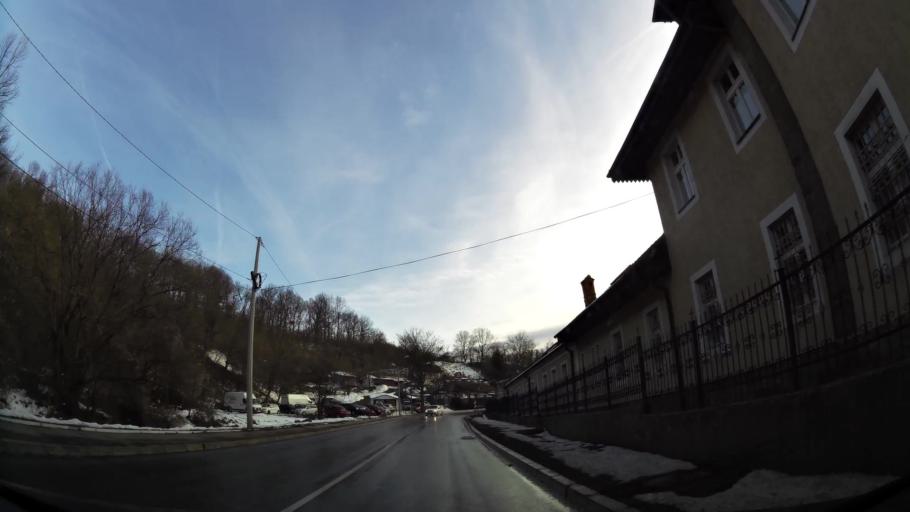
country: RS
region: Central Serbia
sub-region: Belgrade
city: Rakovica
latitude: 44.7309
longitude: 20.4474
